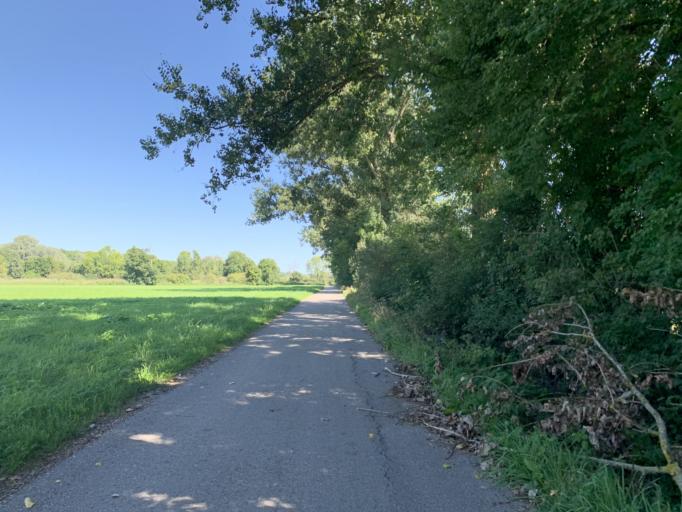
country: DE
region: Bavaria
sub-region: Upper Bavaria
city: Freising
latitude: 48.3784
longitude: 11.7206
